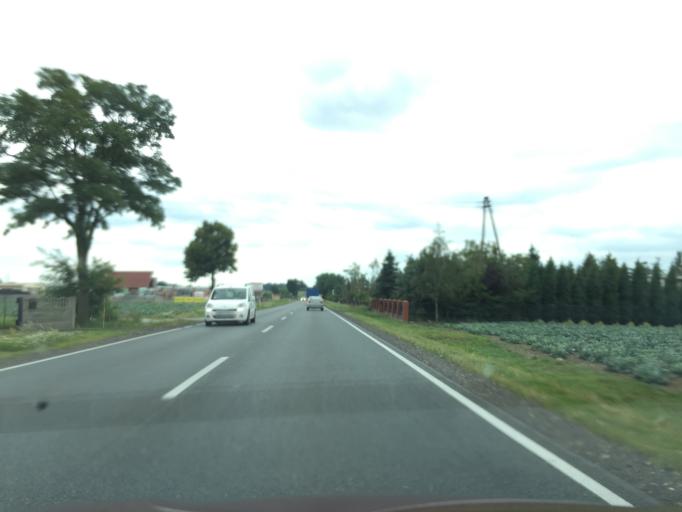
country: PL
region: Greater Poland Voivodeship
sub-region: Kalisz
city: Kalisz
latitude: 51.8281
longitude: 18.0945
